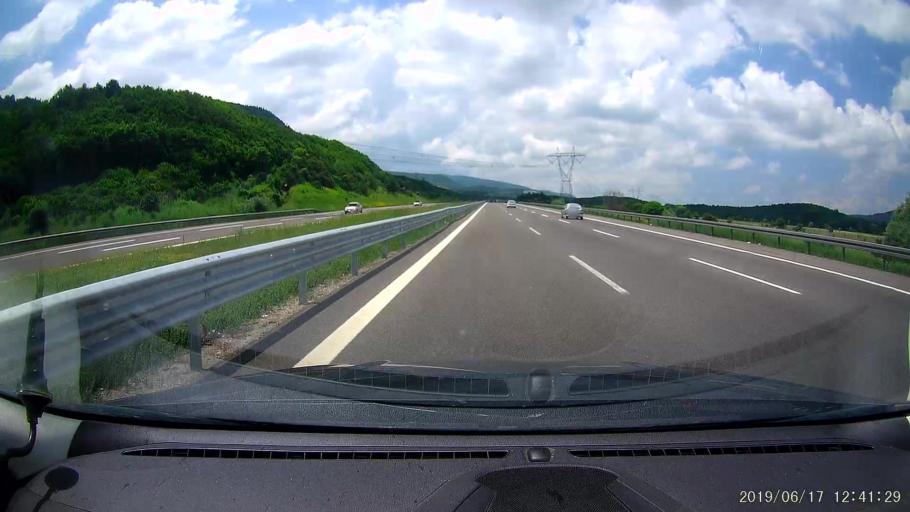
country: TR
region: Bolu
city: Yenicaga
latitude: 40.7595
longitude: 31.9721
